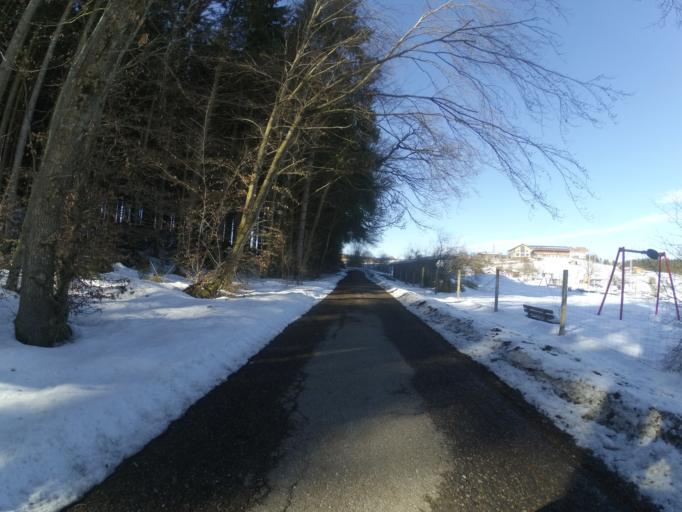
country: DE
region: Bavaria
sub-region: Upper Bavaria
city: Feldkirchen-Westerham
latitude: 47.9271
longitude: 11.8132
